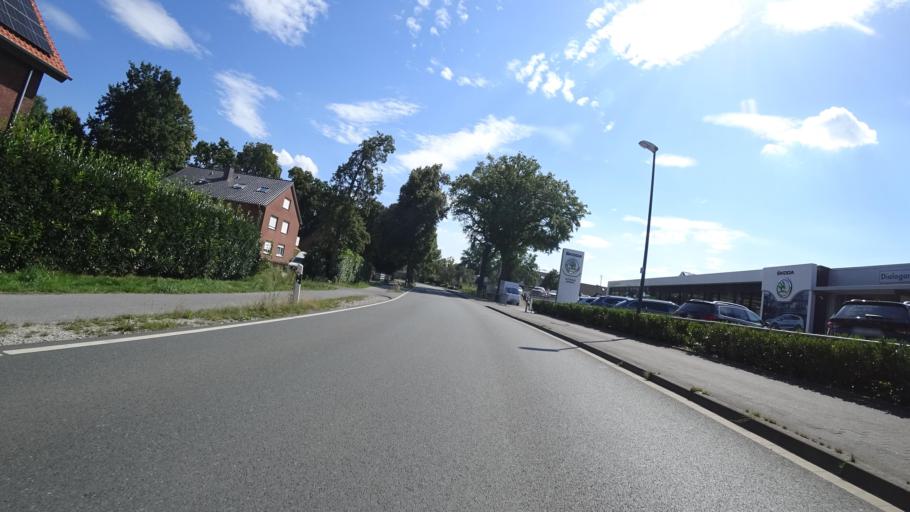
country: DE
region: North Rhine-Westphalia
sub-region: Regierungsbezirk Detmold
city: Guetersloh
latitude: 51.9431
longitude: 8.4123
